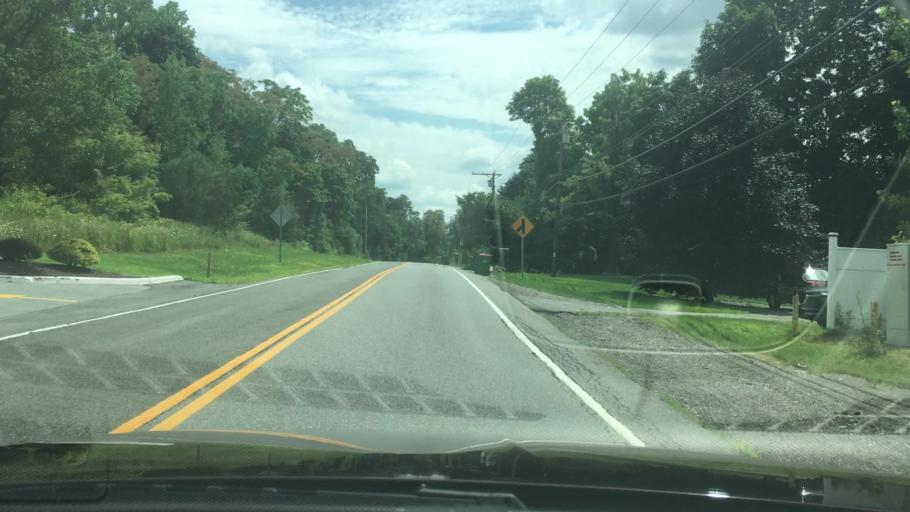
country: US
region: New York
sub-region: Dutchess County
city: Red Oaks Mill
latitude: 41.6579
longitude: -73.8476
